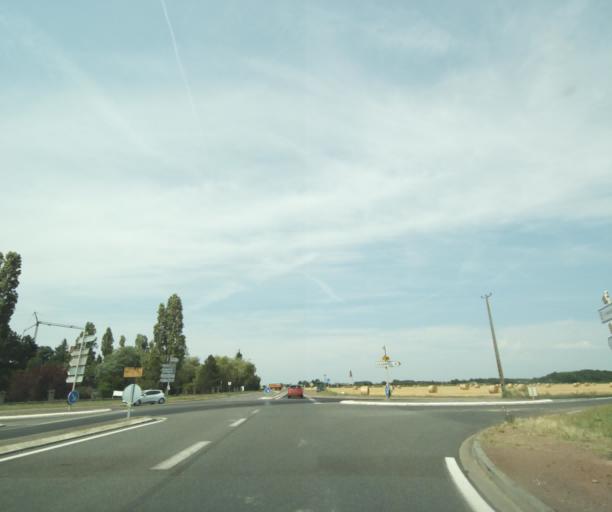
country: FR
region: Centre
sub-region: Departement d'Indre-et-Loire
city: Sorigny
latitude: 47.1990
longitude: 0.6699
